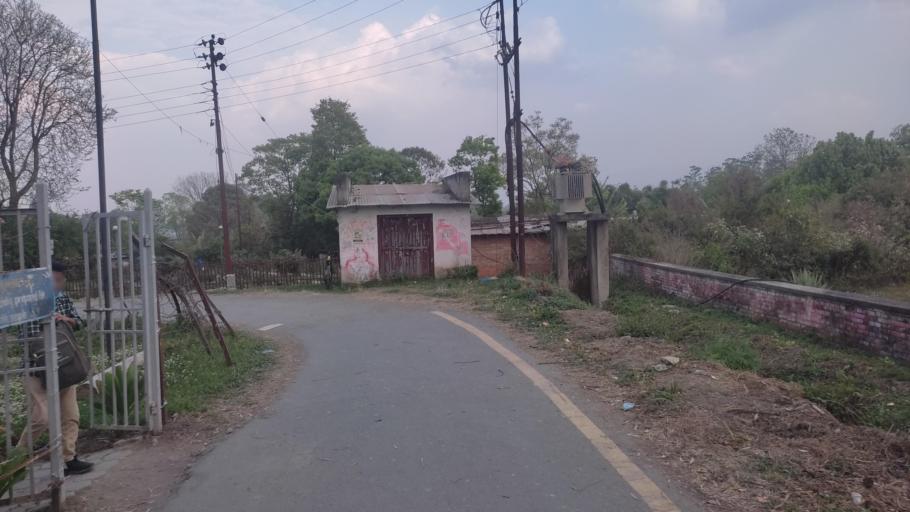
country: NP
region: Central Region
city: Kirtipur
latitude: 27.6813
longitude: 85.2853
